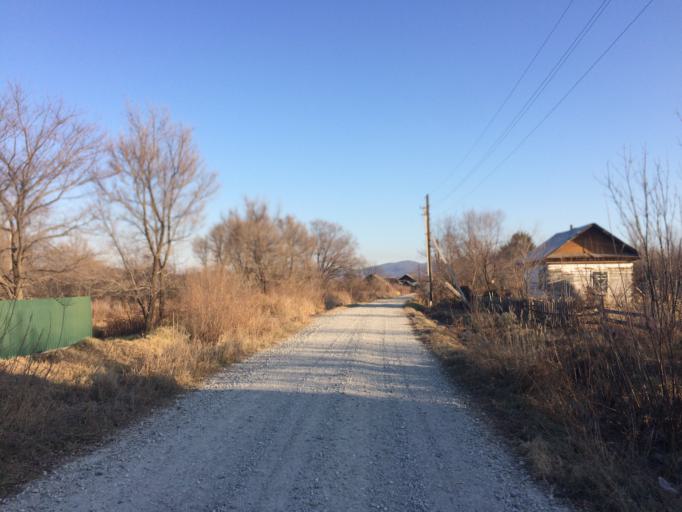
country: RU
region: Primorskiy
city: Ivanovka
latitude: 43.9558
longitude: 132.4823
